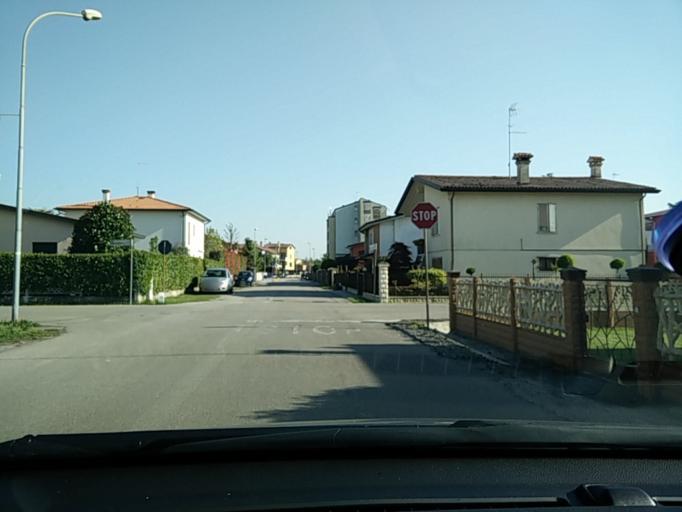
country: IT
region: Veneto
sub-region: Provincia di Venezia
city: San Dona di Piave
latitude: 45.6185
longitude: 12.5659
